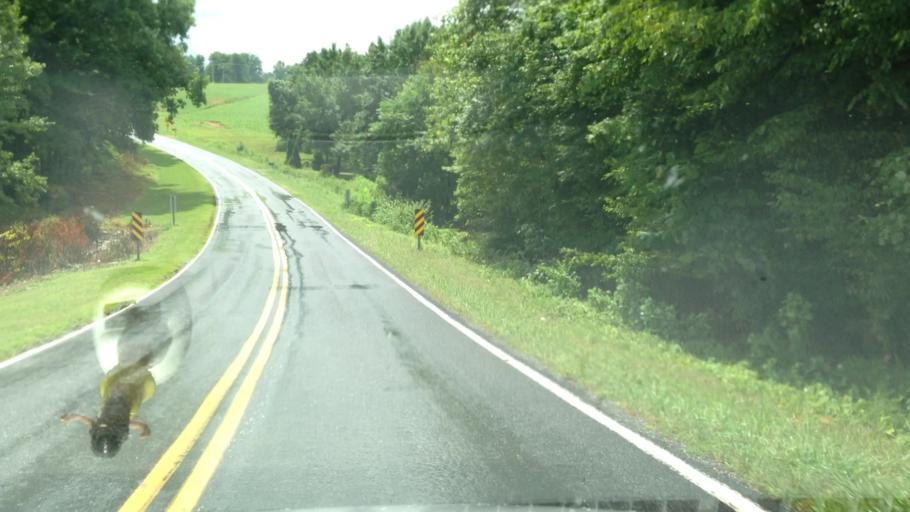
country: US
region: North Carolina
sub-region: Forsyth County
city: Walkertown
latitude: 36.1972
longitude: -80.1004
